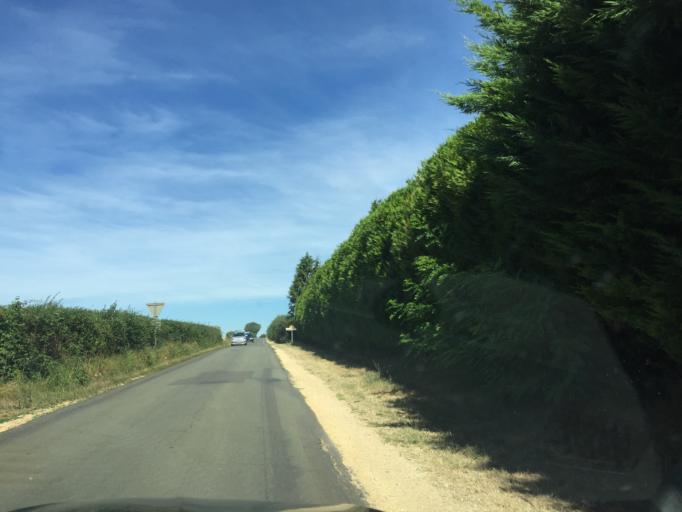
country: FR
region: Poitou-Charentes
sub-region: Departement de la Vienne
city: La Villedieu-du-Clain
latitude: 46.4467
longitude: 0.3313
